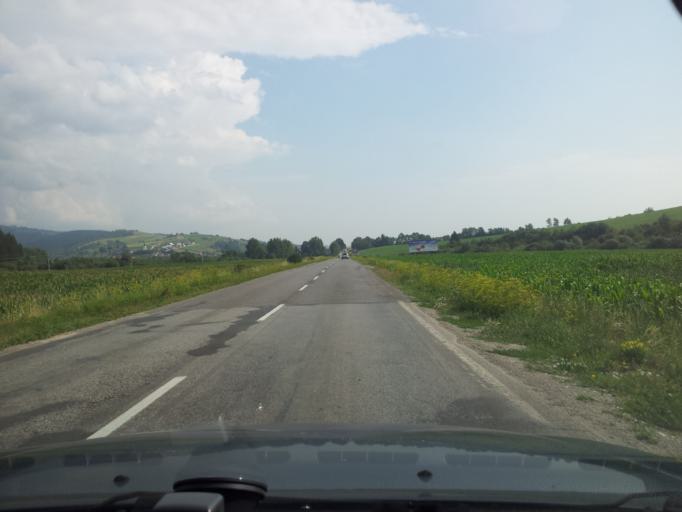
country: SK
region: Zilinsky
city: Namestovo
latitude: 49.3760
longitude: 19.4271
